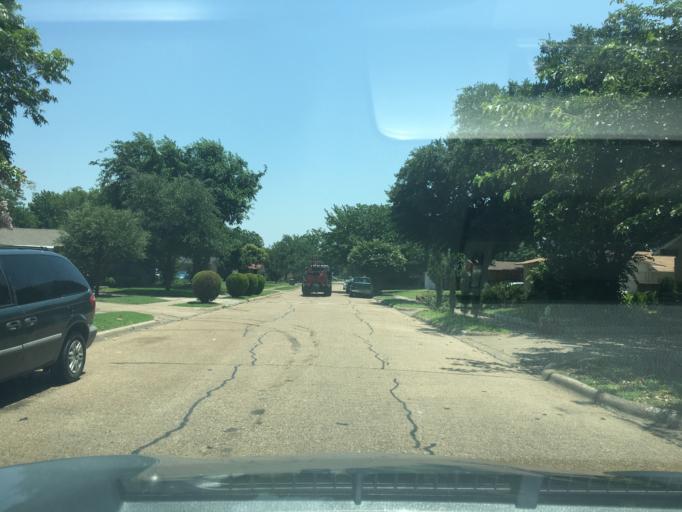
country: US
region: Texas
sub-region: Dallas County
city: Richardson
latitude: 32.9128
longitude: -96.6976
